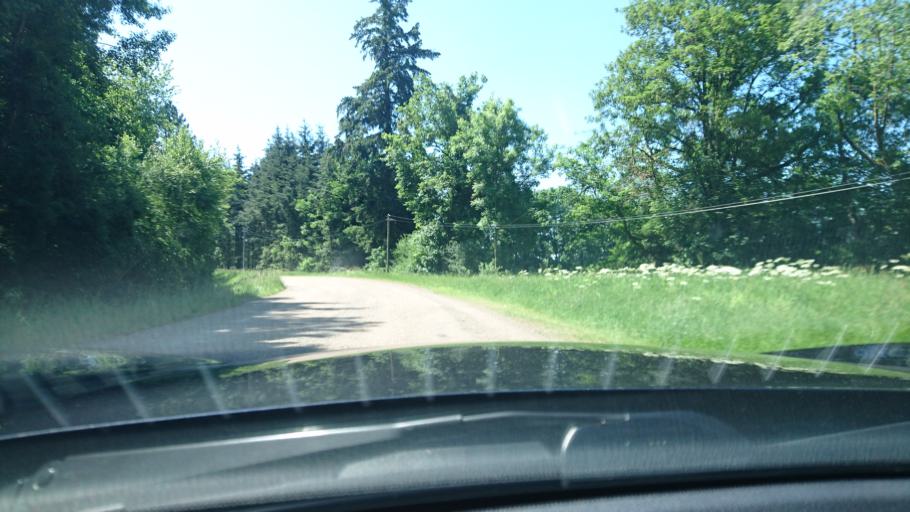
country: FR
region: Rhone-Alpes
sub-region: Departement de la Loire
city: Bussieres
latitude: 45.8502
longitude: 4.2588
